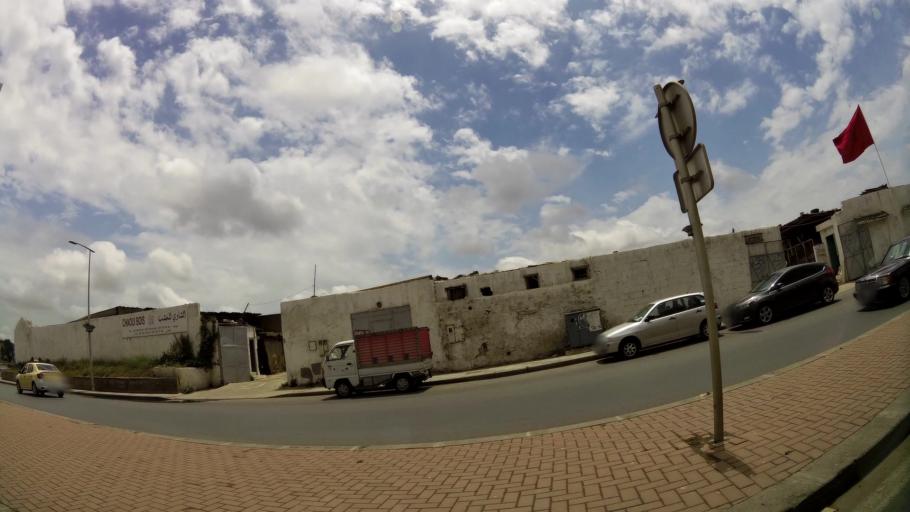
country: MA
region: Rabat-Sale-Zemmour-Zaer
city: Sale
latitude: 34.0349
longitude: -6.8099
